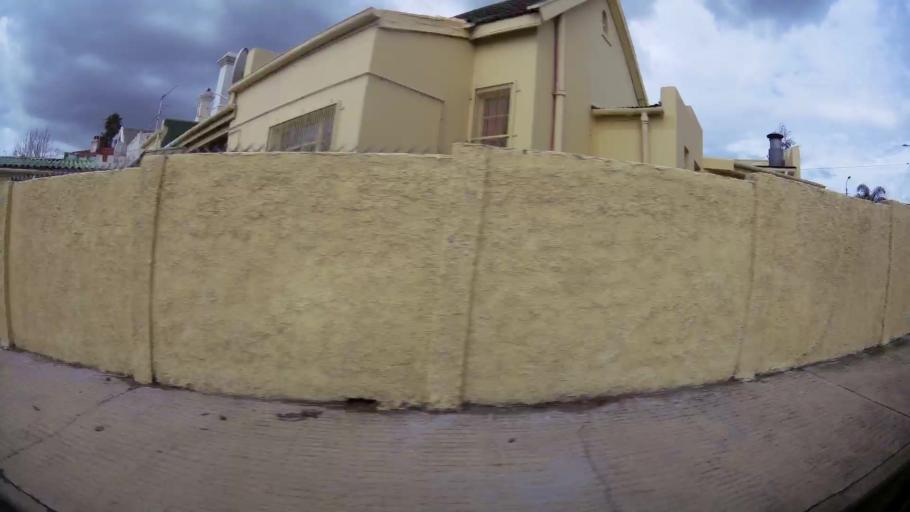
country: ZA
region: Eastern Cape
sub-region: Nelson Mandela Bay Metropolitan Municipality
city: Port Elizabeth
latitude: -33.9575
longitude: 25.5936
